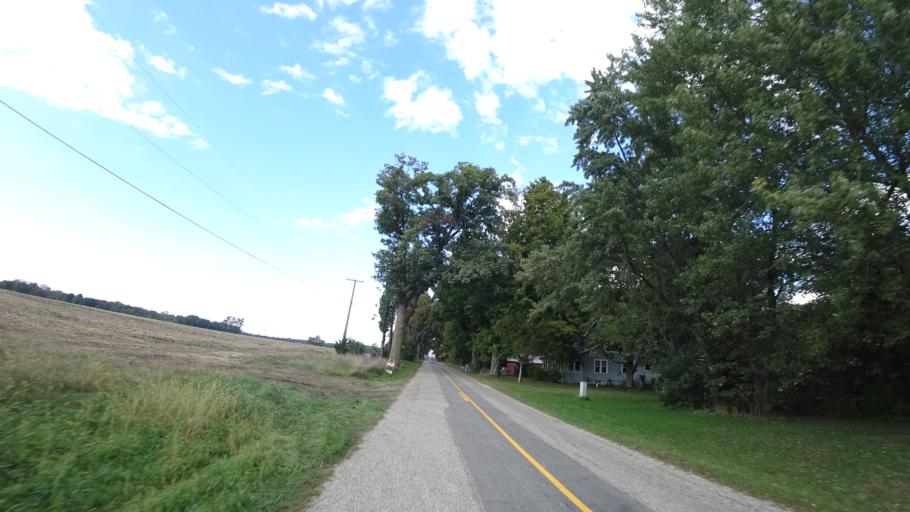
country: US
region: Michigan
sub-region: Saint Joseph County
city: Three Rivers
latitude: 41.9518
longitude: -85.5910
